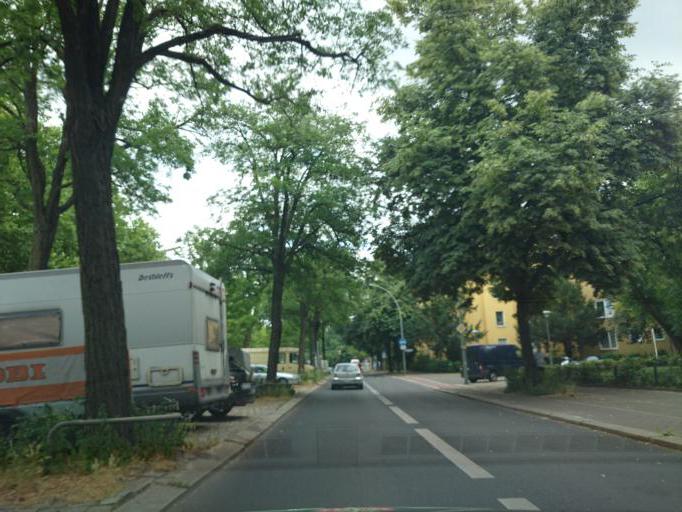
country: DE
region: Berlin
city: Schoneberg Bezirk
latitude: 52.4602
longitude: 13.3463
